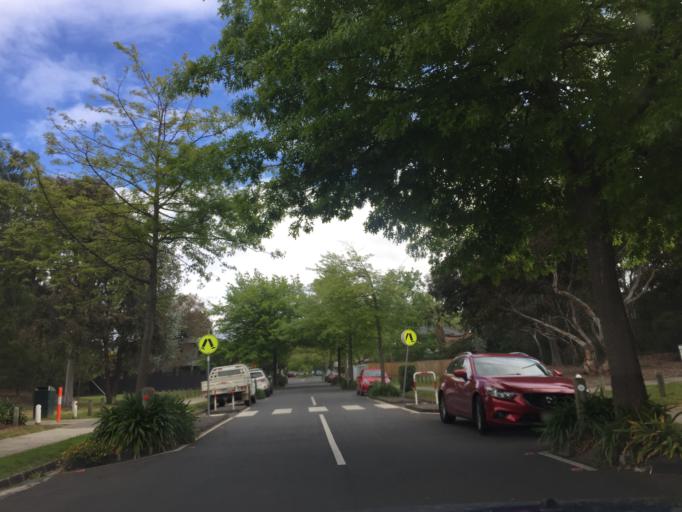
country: AU
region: Victoria
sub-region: Boroondara
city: Kew East
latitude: -37.8007
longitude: 145.0552
